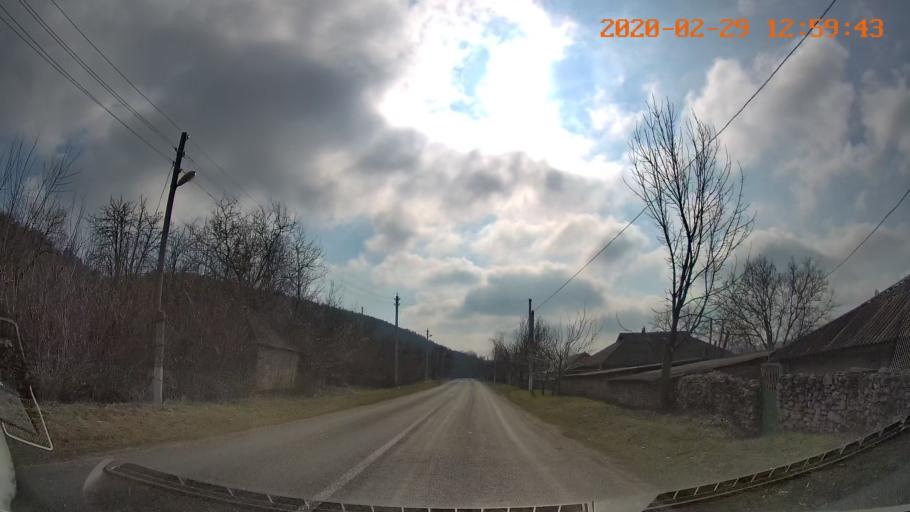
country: MD
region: Telenesti
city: Camenca
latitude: 48.0594
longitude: 28.7251
